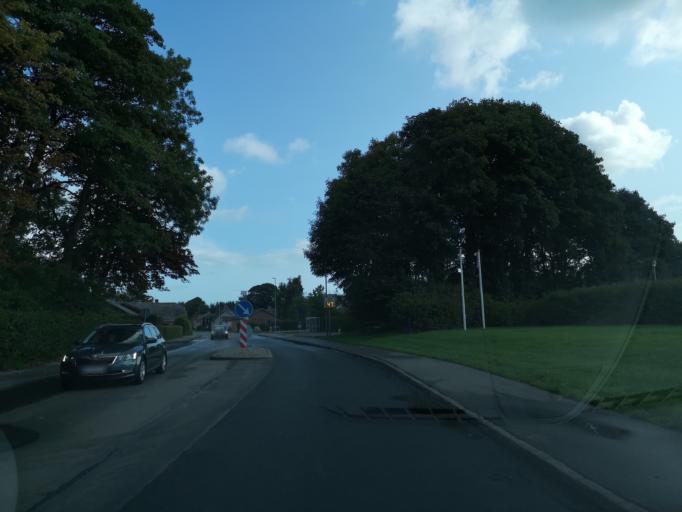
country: DK
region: Central Jutland
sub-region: Ringkobing-Skjern Kommune
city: Videbaek
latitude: 56.0439
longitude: 8.6196
